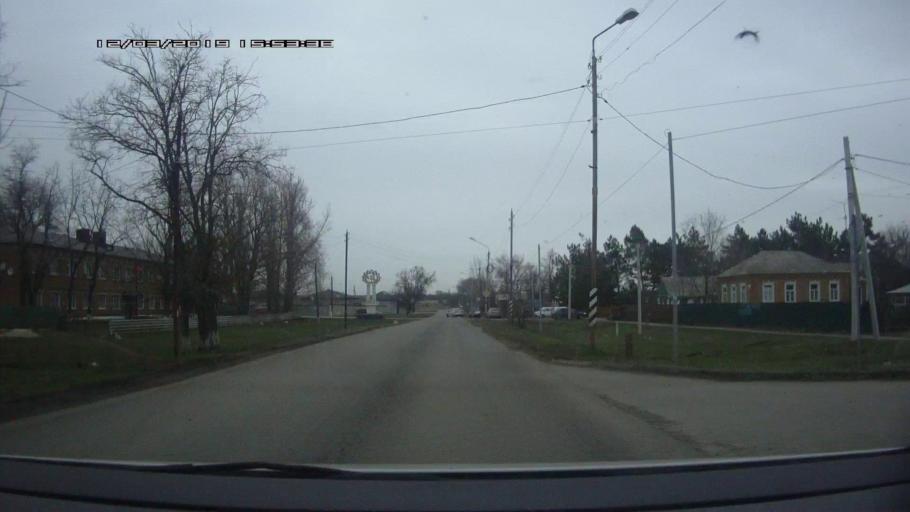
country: RU
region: Rostov
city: Novobataysk
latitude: 46.8861
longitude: 39.7764
